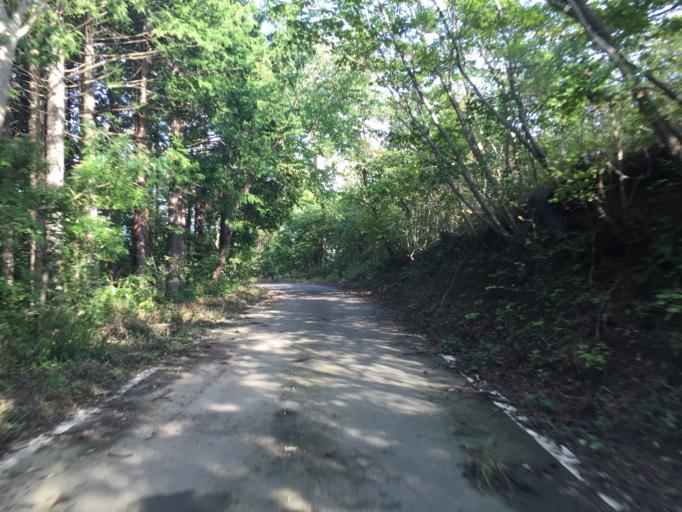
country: JP
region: Fukushima
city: Yanagawamachi-saiwaicho
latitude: 37.8993
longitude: 140.5433
